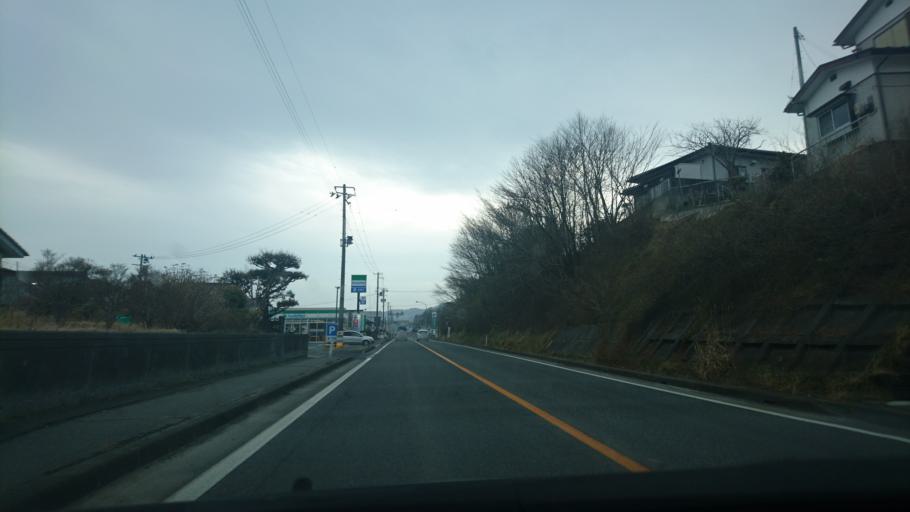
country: JP
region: Iwate
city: Ofunato
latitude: 39.0400
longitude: 141.7207
